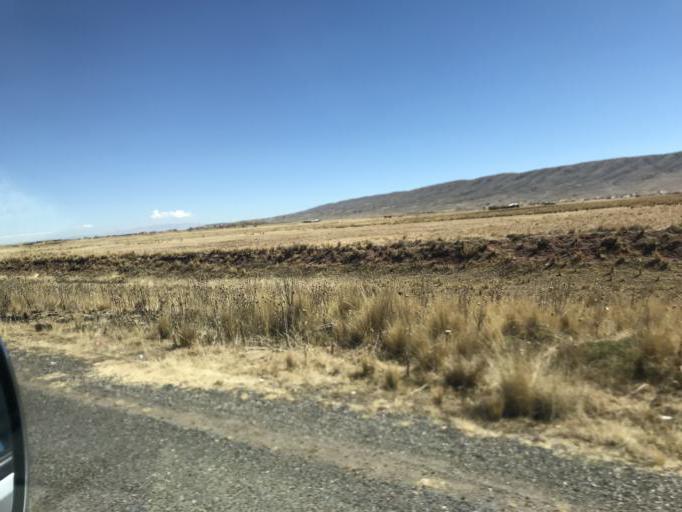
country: BO
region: La Paz
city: Tiahuanaco
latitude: -16.5677
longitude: -68.6538
